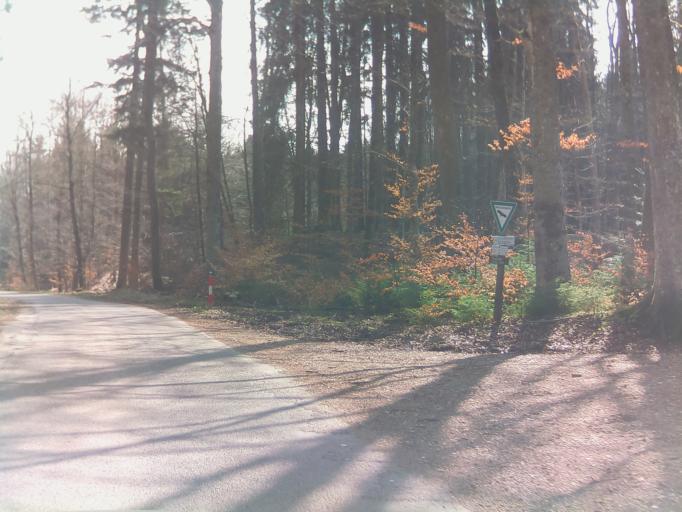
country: DE
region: Baden-Wuerttemberg
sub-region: Tuebingen Region
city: Gomadingen
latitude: 48.4366
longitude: 9.4234
